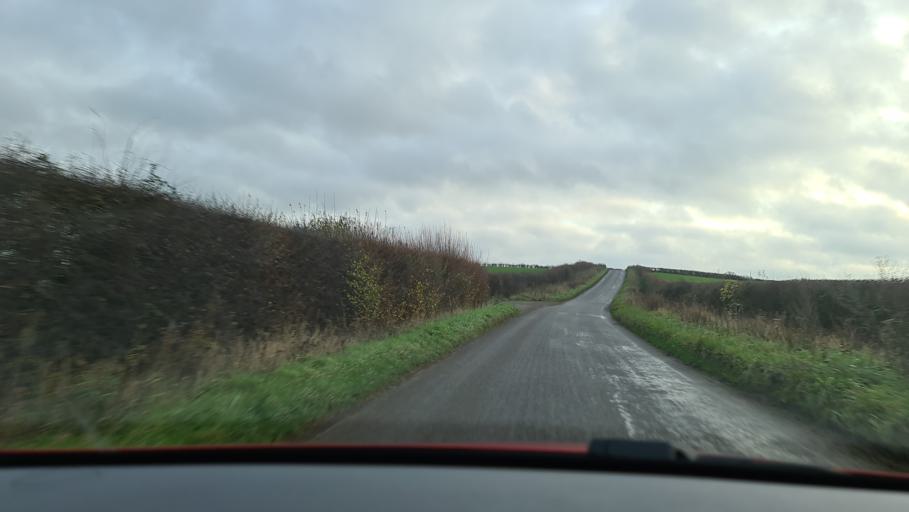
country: GB
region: England
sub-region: Buckinghamshire
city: Long Crendon
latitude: 51.7978
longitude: -0.9767
